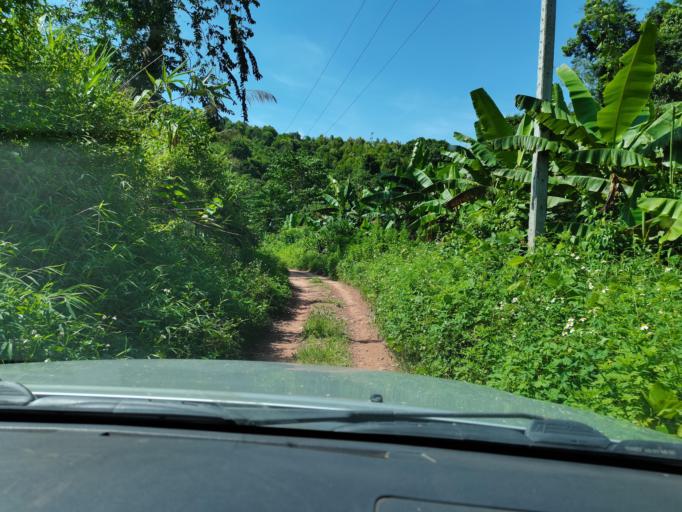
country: LA
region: Loungnamtha
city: Muang Nale
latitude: 20.5435
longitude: 101.0628
